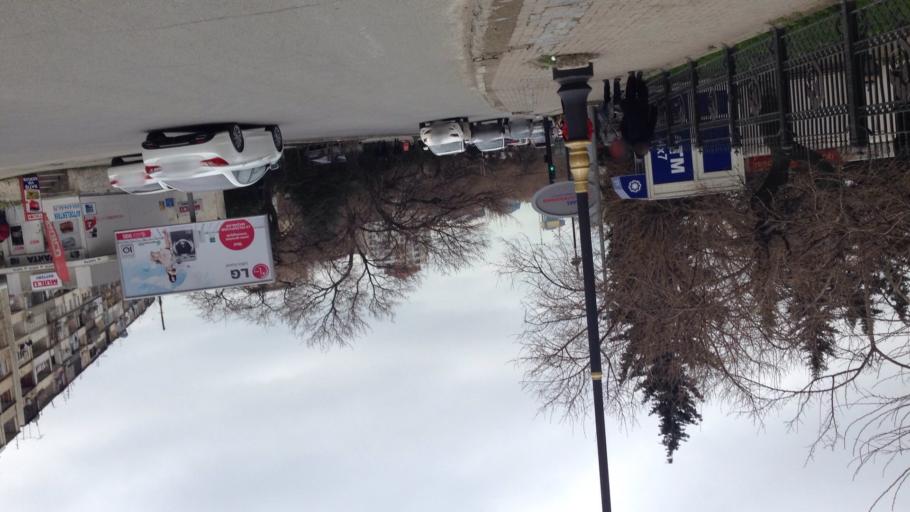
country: AZ
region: Baki
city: Baku
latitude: 40.3896
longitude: 49.8499
